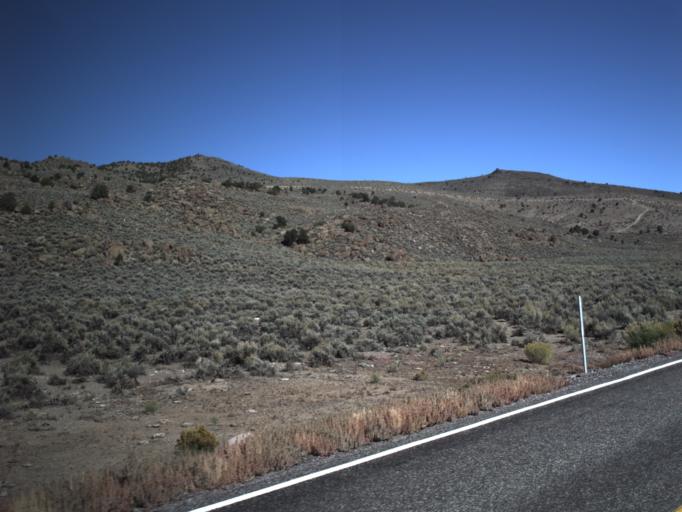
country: US
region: Utah
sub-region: Piute County
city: Junction
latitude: 38.1722
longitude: -112.0270
